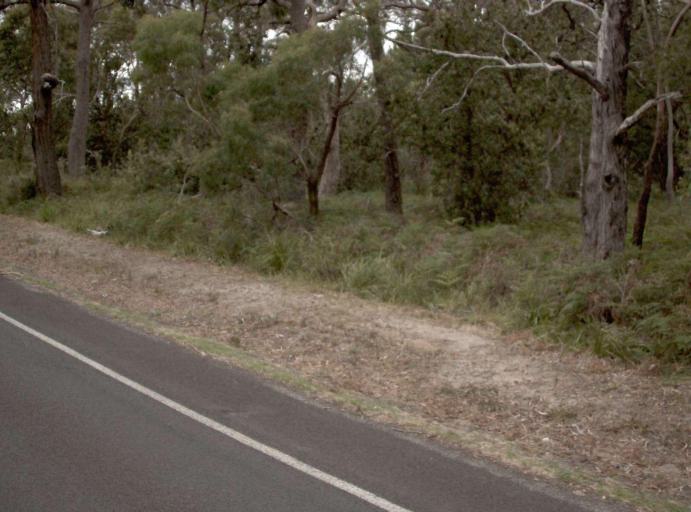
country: AU
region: Victoria
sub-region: Wellington
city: Sale
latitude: -38.2301
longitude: 147.0549
